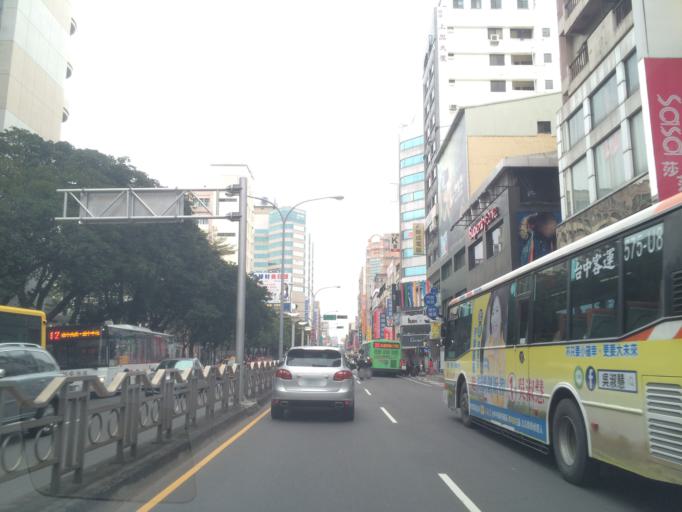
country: TW
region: Taiwan
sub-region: Taichung City
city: Taichung
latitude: 24.1492
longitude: 120.6839
